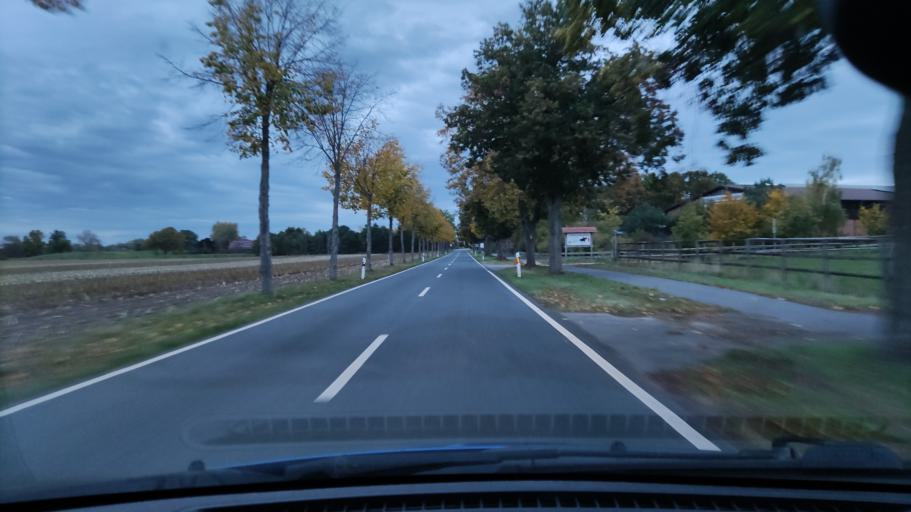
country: DE
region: Lower Saxony
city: Gorleben
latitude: 53.0639
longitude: 11.3987
